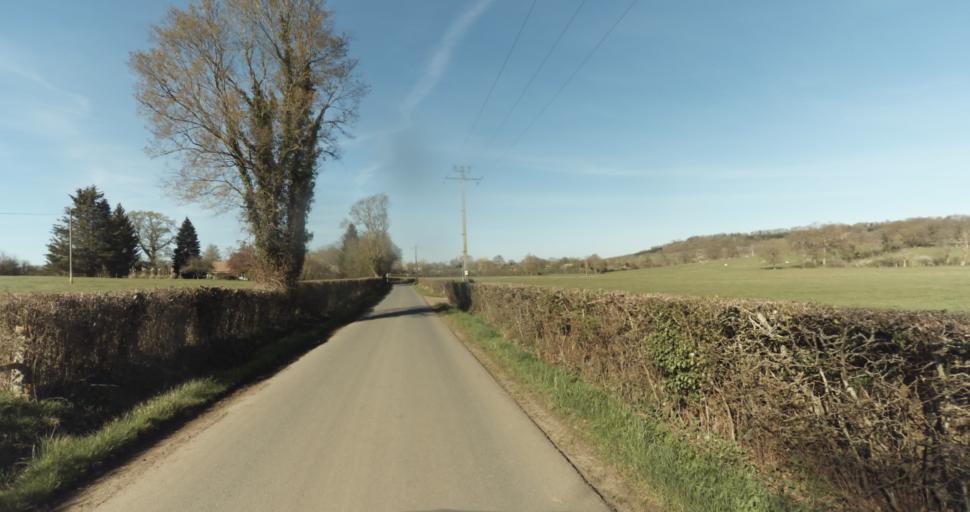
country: FR
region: Lower Normandy
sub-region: Departement du Calvados
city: Saint-Pierre-sur-Dives
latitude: 49.0249
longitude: 0.0556
